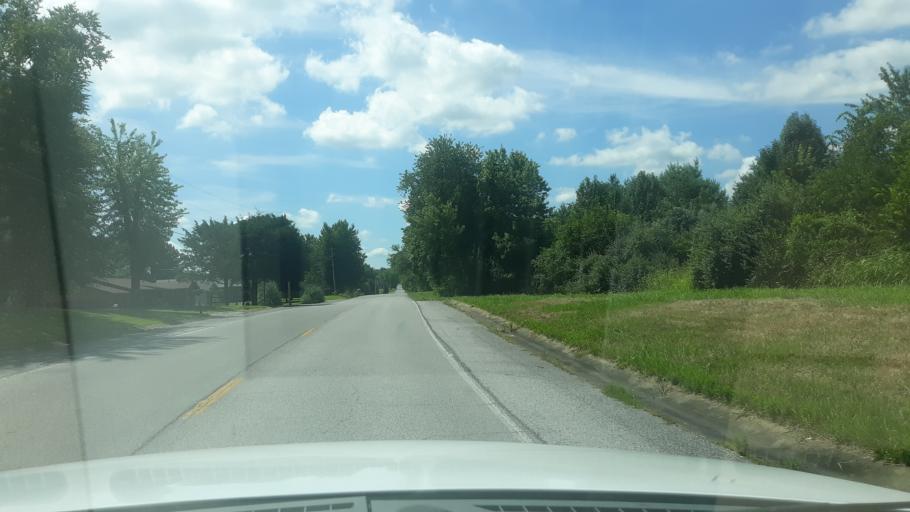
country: US
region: Illinois
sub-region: Saline County
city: Harrisburg
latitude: 37.7327
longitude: -88.5689
